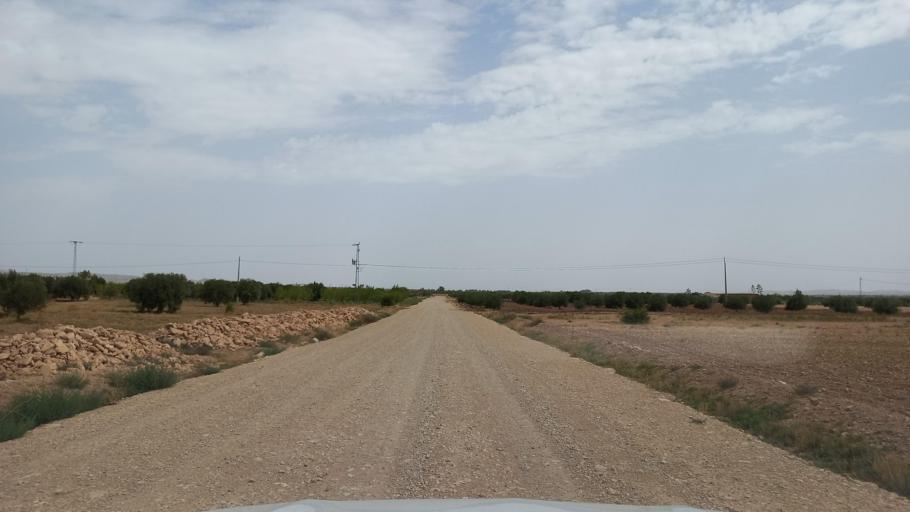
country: TN
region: Al Qasrayn
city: Kasserine
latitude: 35.2784
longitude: 9.0172
